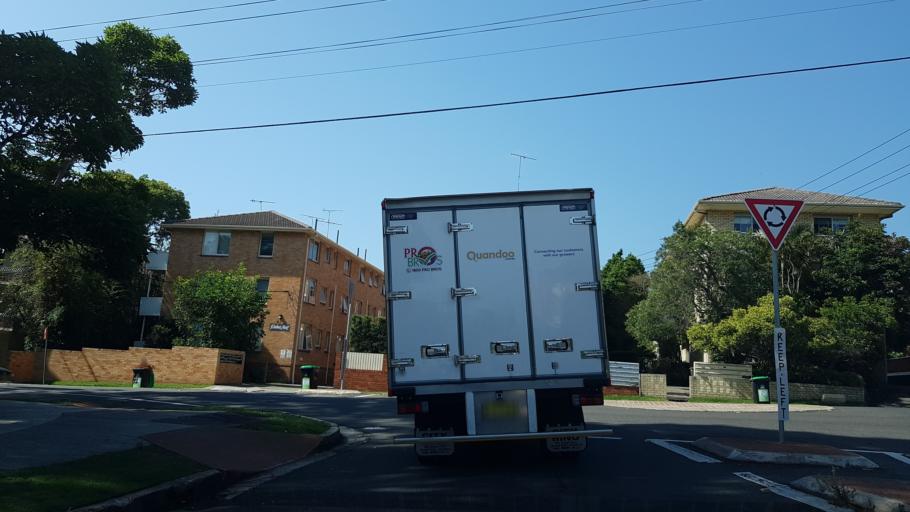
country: AU
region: New South Wales
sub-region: Warringah
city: North Curl Curl
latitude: -33.7552
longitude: 151.2919
